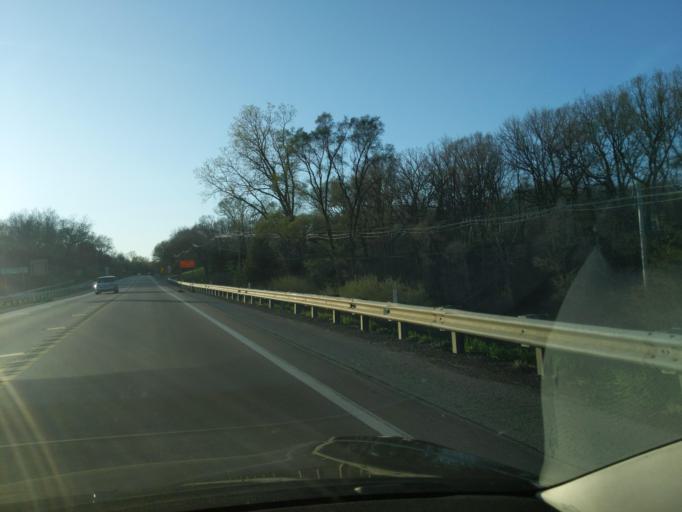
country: US
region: Michigan
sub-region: Washtenaw County
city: Chelsea
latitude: 42.3378
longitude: -84.0304
